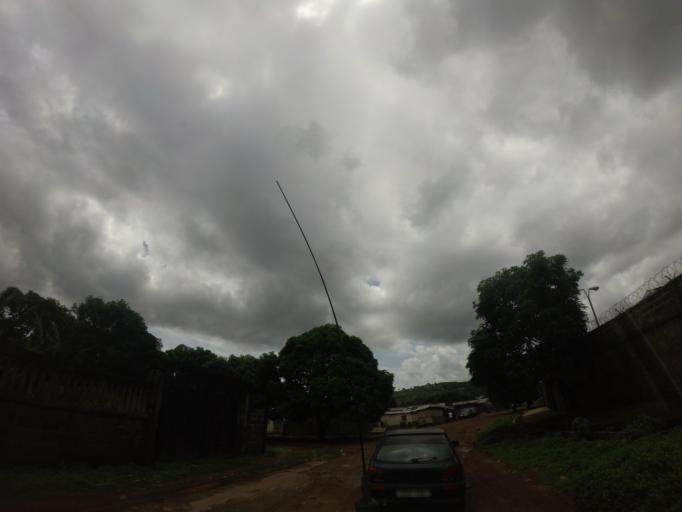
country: SL
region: Western Area
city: Hastings
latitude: 8.3813
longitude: -13.1336
